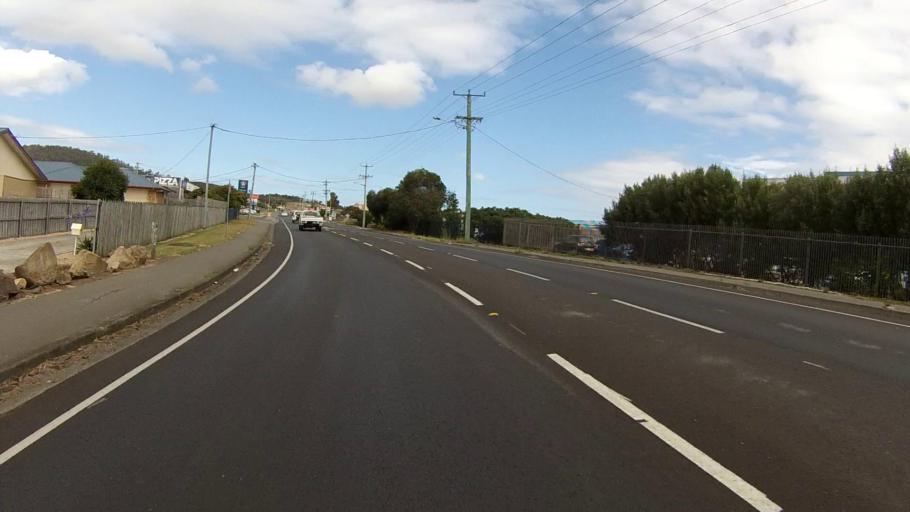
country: AU
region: Tasmania
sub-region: Clarence
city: Rokeby
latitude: -42.9012
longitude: 147.4454
